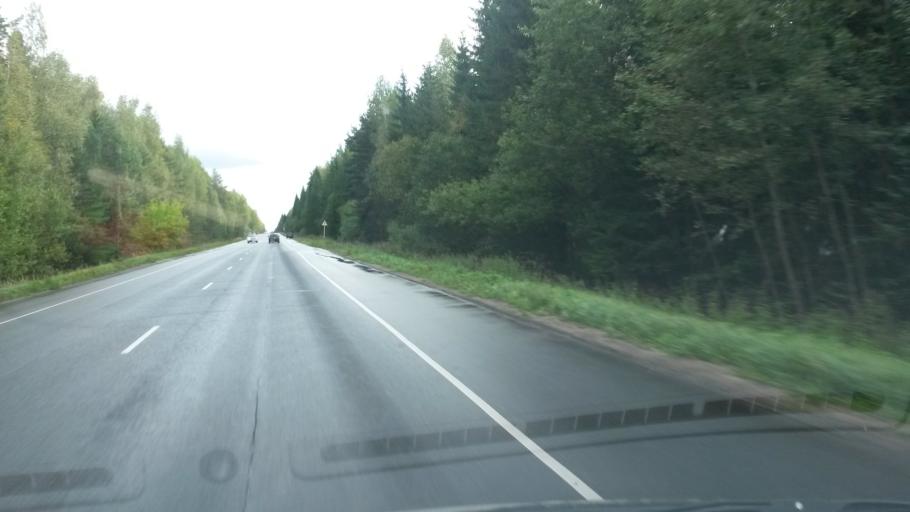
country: RU
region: Ivanovo
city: Kaminskiy
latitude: 57.0394
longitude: 41.3336
